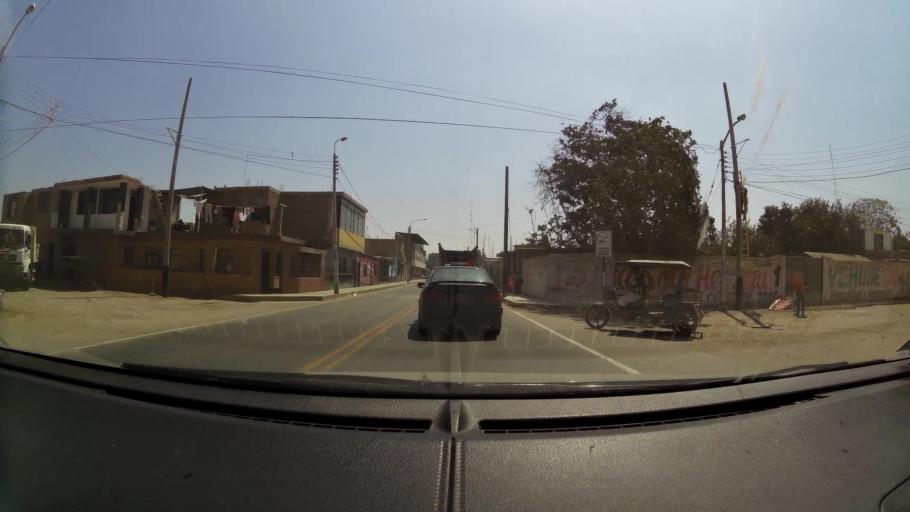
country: PE
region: Lambayeque
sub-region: Provincia de Chiclayo
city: Mocupe
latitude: -6.9911
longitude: -79.6209
